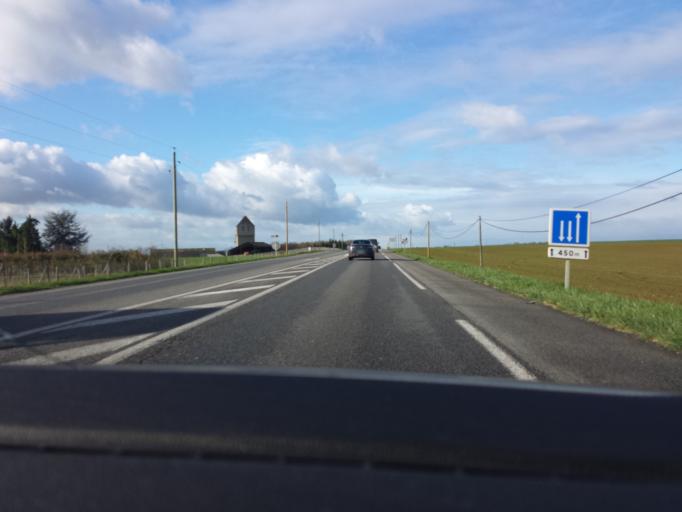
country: FR
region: Haute-Normandie
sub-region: Departement de l'Eure
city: Menilles
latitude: 49.0123
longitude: 1.3073
